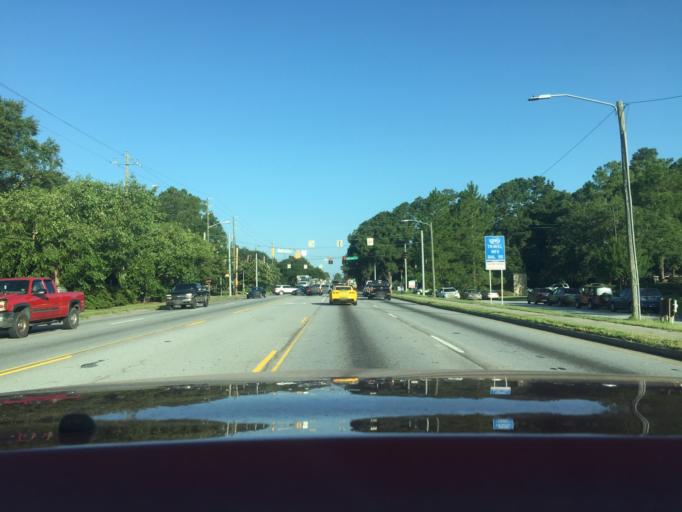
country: US
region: Georgia
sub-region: Chatham County
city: Thunderbolt
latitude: 32.0273
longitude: -81.1049
